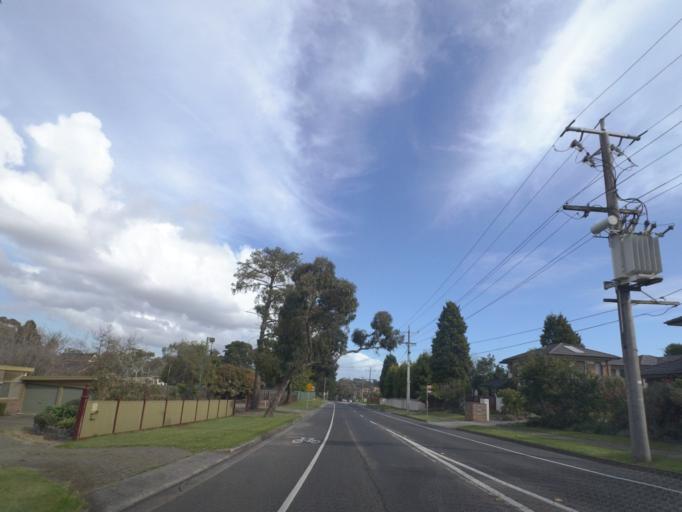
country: AU
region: Victoria
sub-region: Whitehorse
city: Vermont South
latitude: -37.8479
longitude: 145.1890
